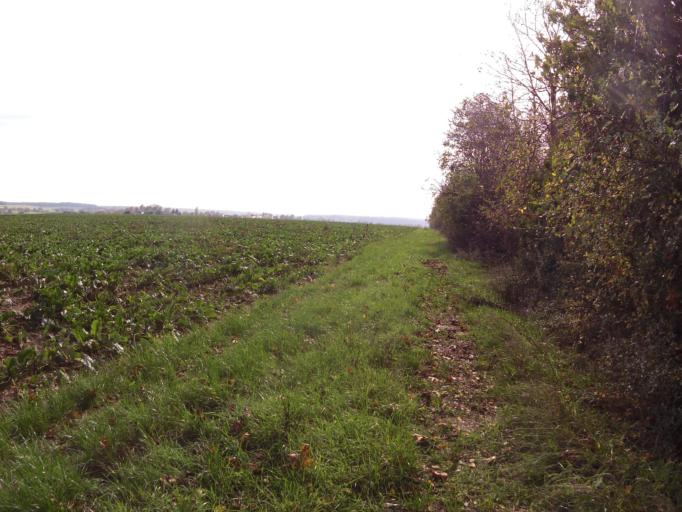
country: DE
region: Bavaria
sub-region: Regierungsbezirk Unterfranken
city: Frickenhausen
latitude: 49.7136
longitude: 10.0732
